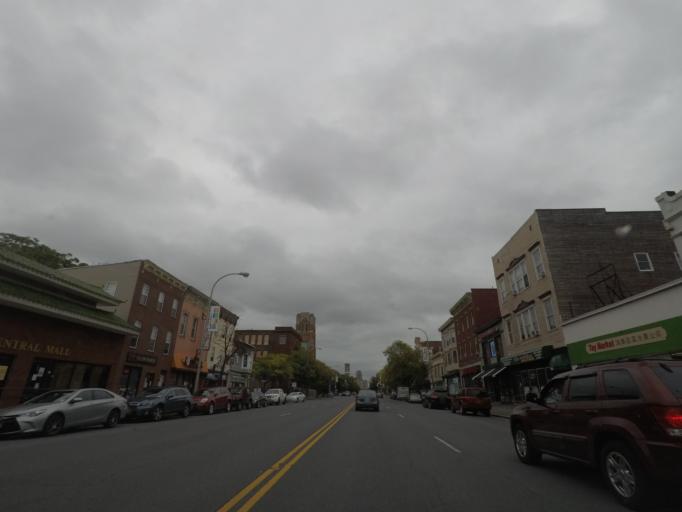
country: US
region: New York
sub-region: Albany County
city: West Albany
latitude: 42.6647
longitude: -73.7724
